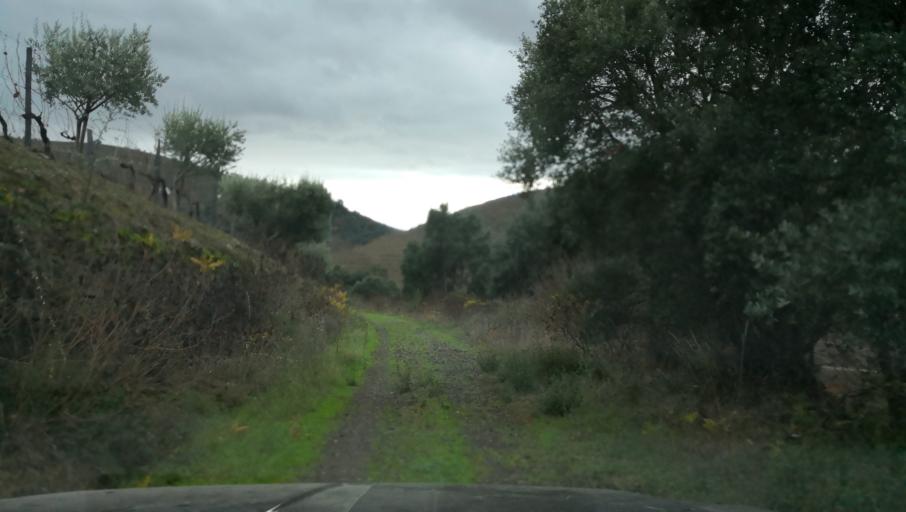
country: PT
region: Vila Real
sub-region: Peso da Regua
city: Peso da Regua
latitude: 41.1840
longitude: -7.7599
